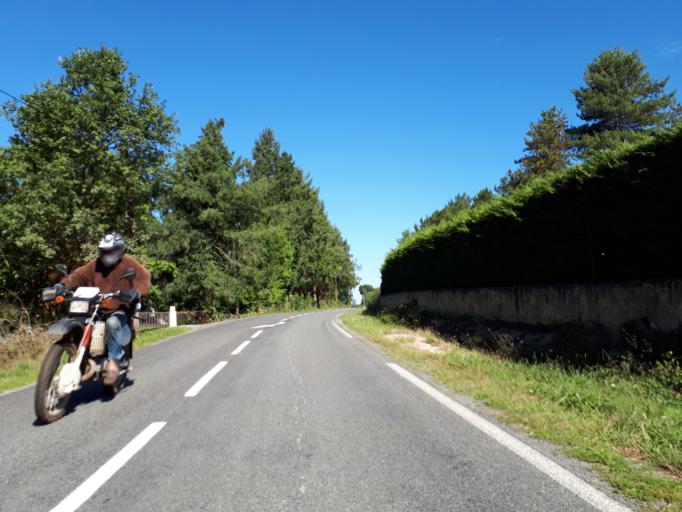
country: FR
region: Rhone-Alpes
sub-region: Departement de la Loire
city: Civens
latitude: 45.7634
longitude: 4.2671
